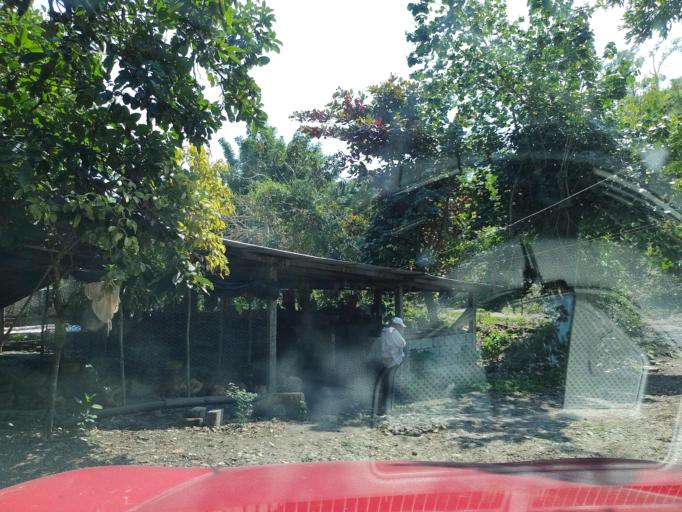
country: MX
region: Veracruz
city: Agua Dulce
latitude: 20.3384
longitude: -97.2009
